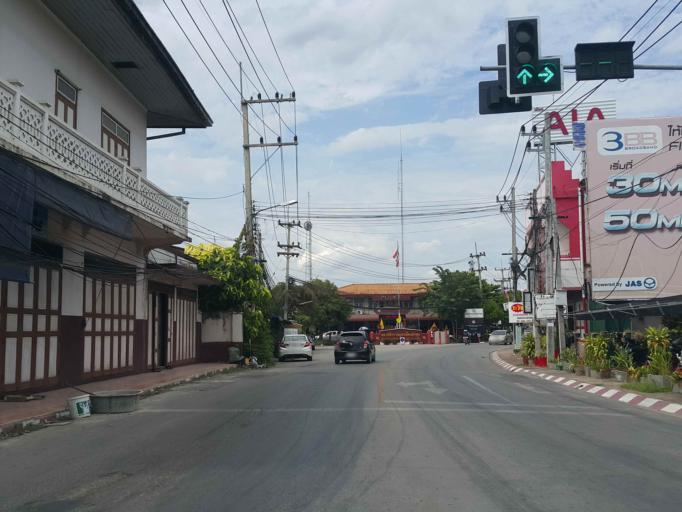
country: TH
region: Lamphun
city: Lamphun
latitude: 18.5820
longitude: 99.0081
